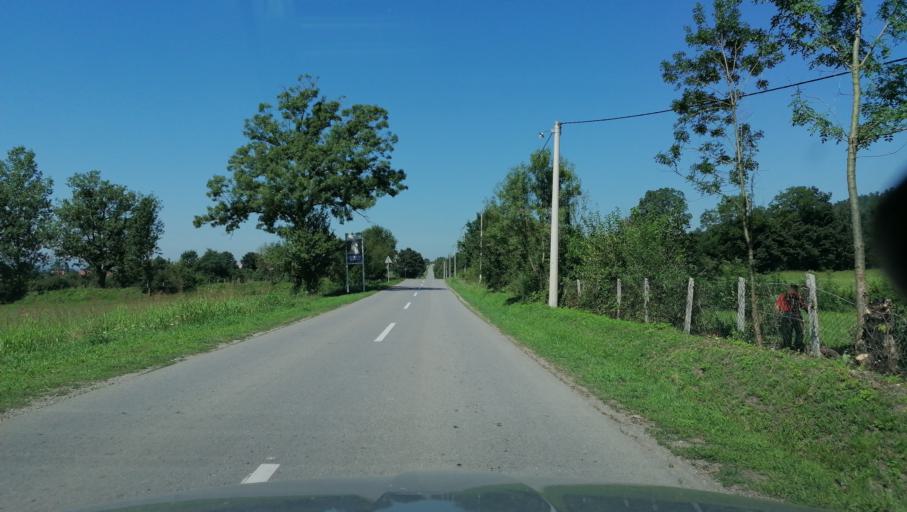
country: RS
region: Central Serbia
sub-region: Raski Okrug
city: Vrnjacka Banja
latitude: 43.6834
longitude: 20.8870
